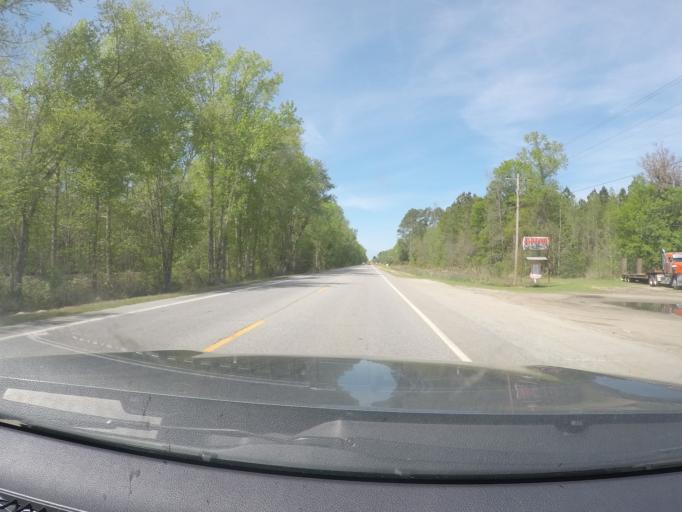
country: US
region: Georgia
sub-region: Bryan County
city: Pembroke
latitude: 32.1341
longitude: -81.5975
